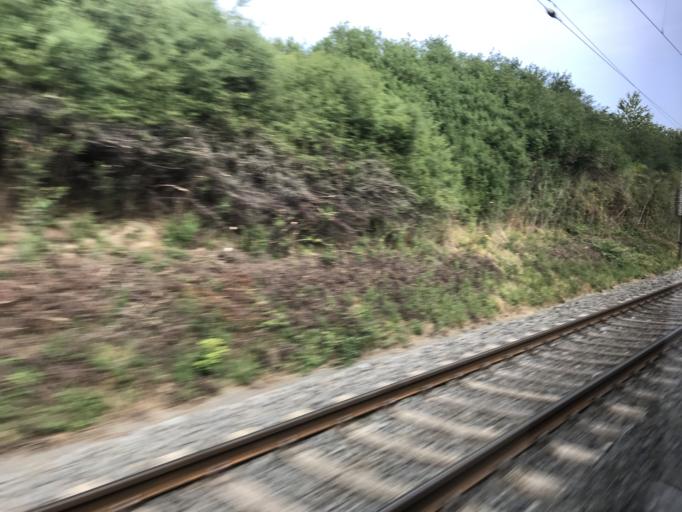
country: DE
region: Hesse
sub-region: Regierungsbezirk Darmstadt
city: Idstein
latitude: 50.2312
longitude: 8.2580
